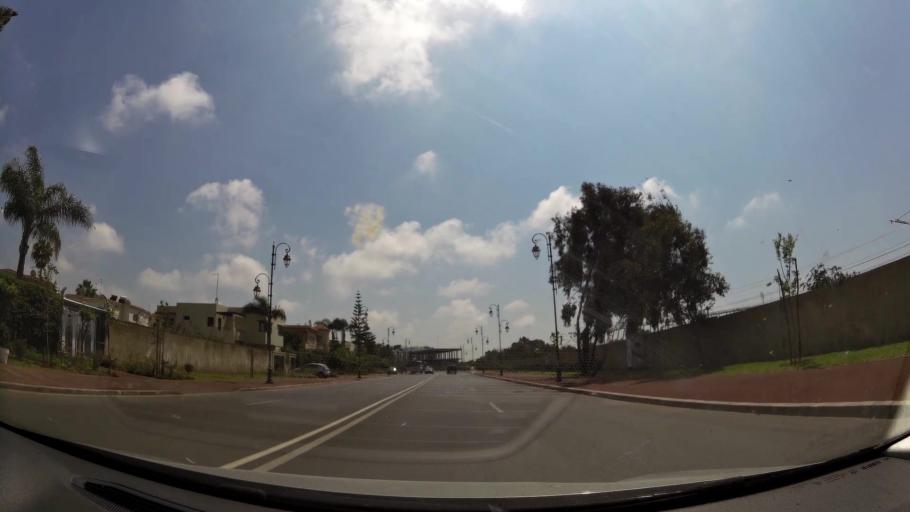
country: MA
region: Rabat-Sale-Zemmour-Zaer
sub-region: Skhirate-Temara
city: Temara
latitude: 33.9615
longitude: -6.8836
